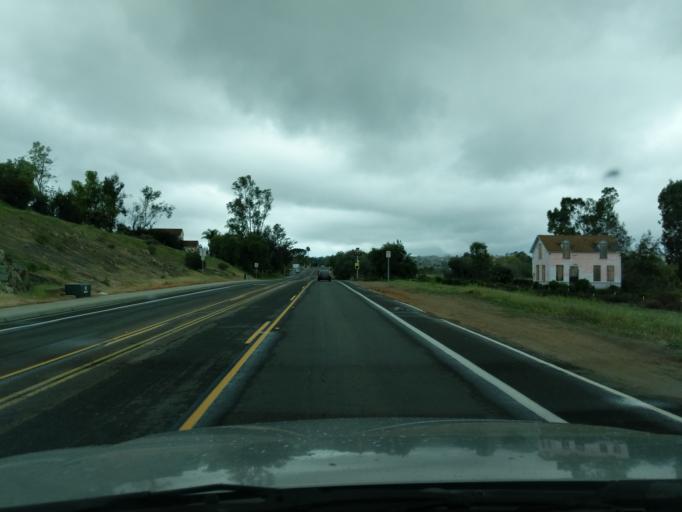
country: US
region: California
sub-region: San Diego County
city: Lake San Marcos
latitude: 33.1303
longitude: -117.1885
